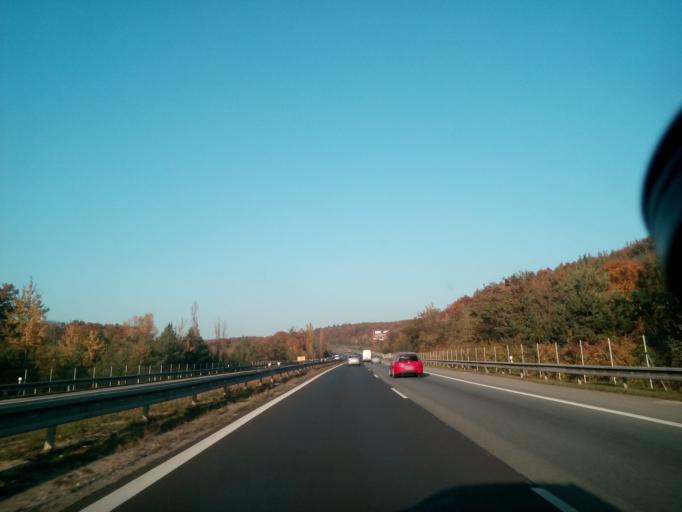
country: SK
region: Kosicky
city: Kosice
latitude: 48.7622
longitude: 21.2867
